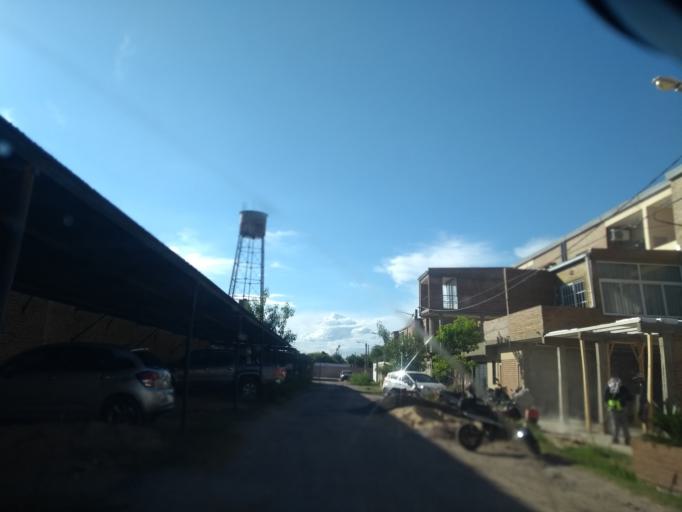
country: AR
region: Chaco
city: Resistencia
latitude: -27.4754
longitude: -58.9620
